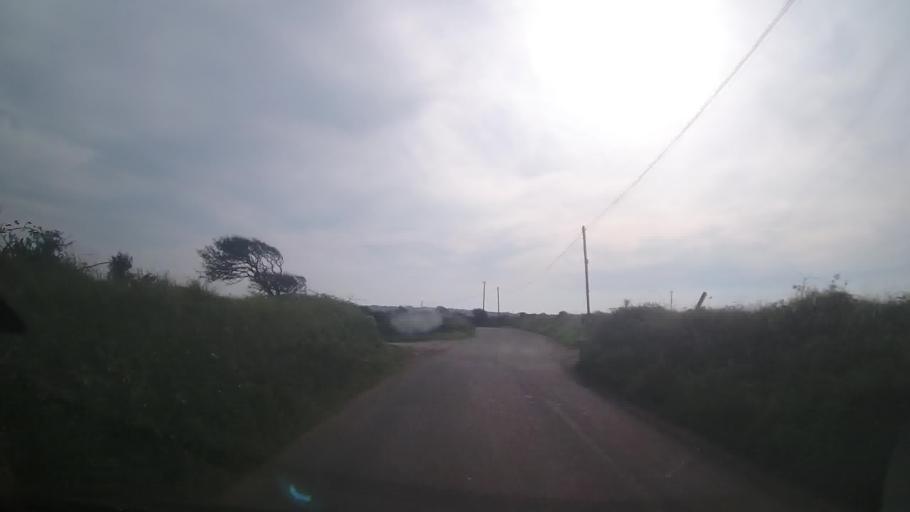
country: GB
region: Wales
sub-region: Pembrokeshire
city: Saint David's
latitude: 51.9077
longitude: -5.2415
